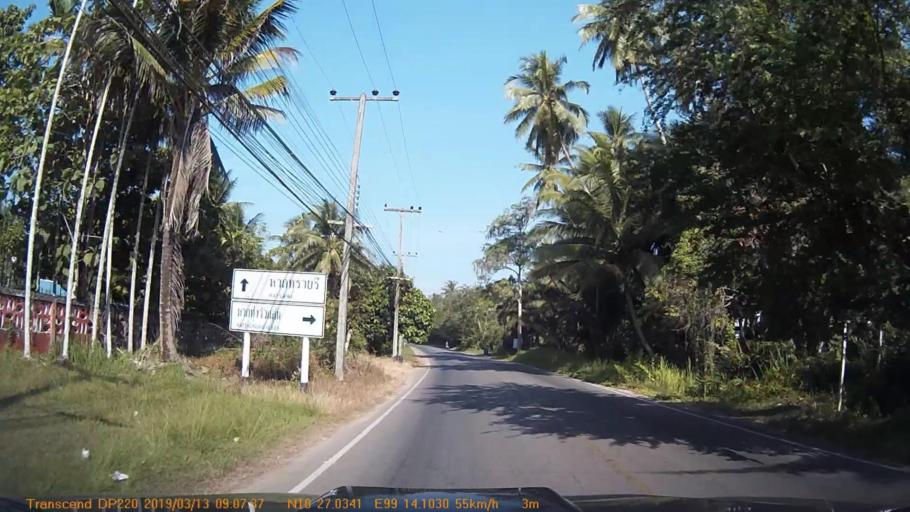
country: TH
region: Chumphon
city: Chumphon
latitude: 10.4507
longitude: 99.2347
